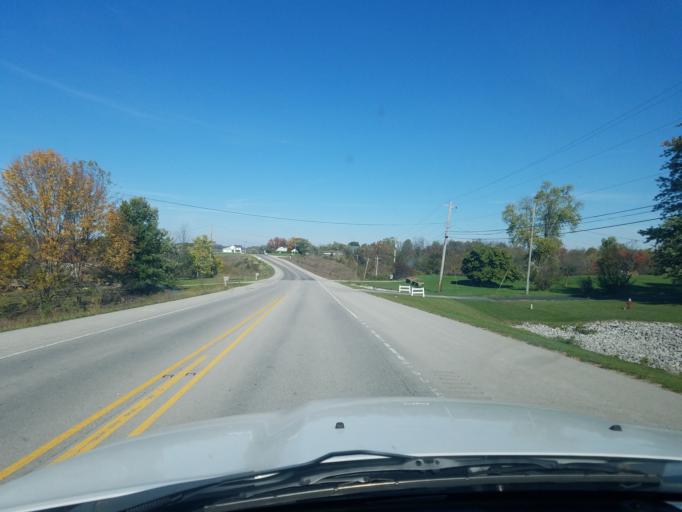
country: US
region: Indiana
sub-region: Washington County
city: Salem
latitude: 38.5896
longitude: -86.0982
